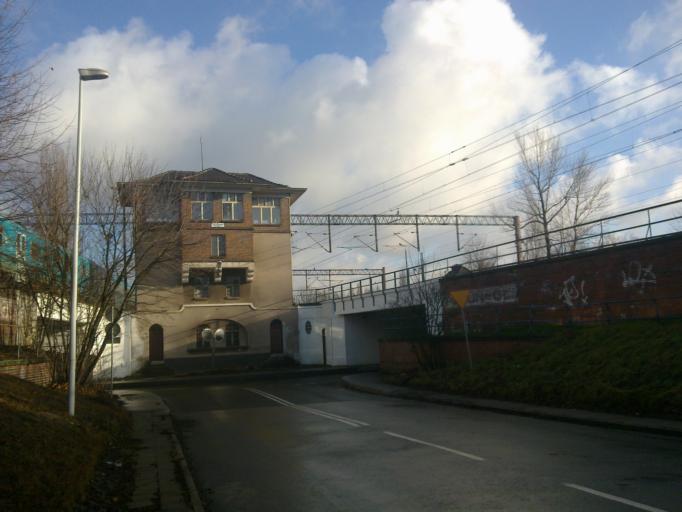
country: PL
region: Kujawsko-Pomorskie
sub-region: Torun
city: Torun
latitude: 53.0013
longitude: 18.6184
